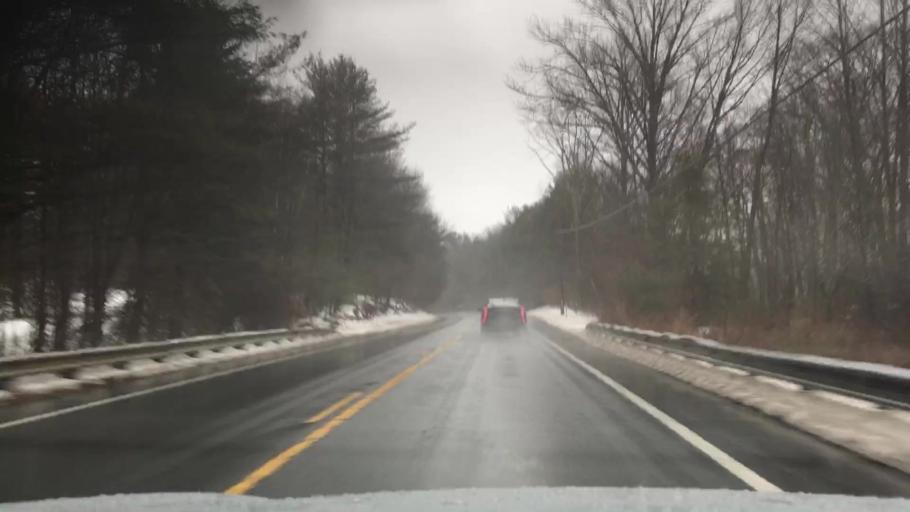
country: US
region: Massachusetts
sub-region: Franklin County
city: Shutesbury
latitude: 42.4844
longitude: -72.3426
